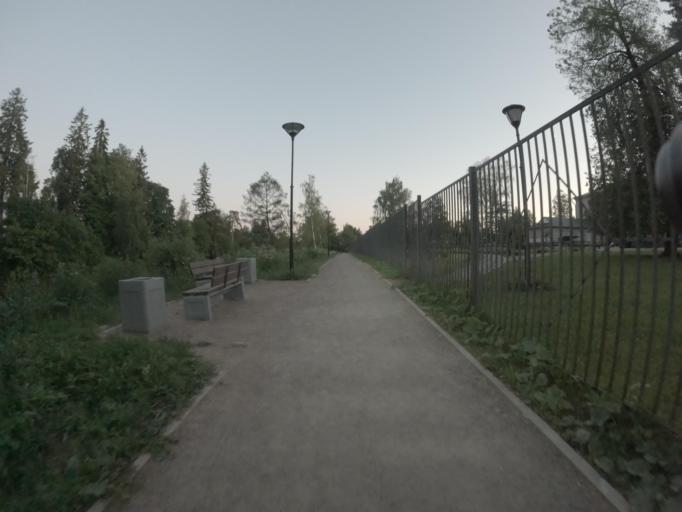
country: RU
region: Leningrad
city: Vsevolozhsk
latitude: 60.0154
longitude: 30.6132
